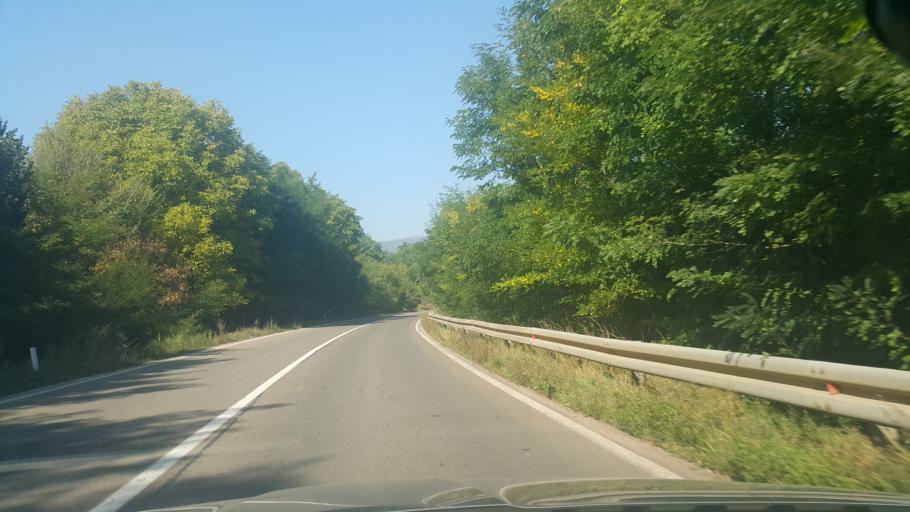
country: RS
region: Central Serbia
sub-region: Pirotski Okrug
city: Bela Palanka
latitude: 43.2536
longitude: 22.2622
